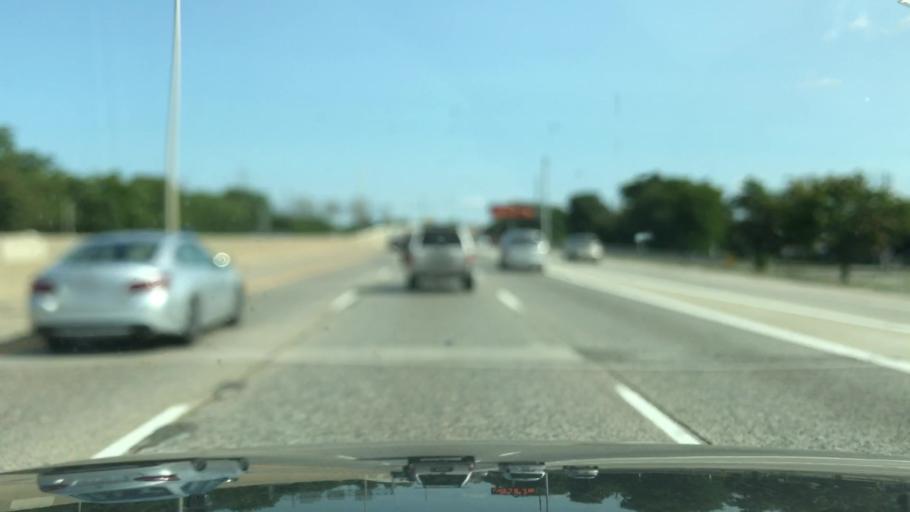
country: US
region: Michigan
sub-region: Kent County
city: Grand Rapids
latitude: 42.9878
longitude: -85.6770
